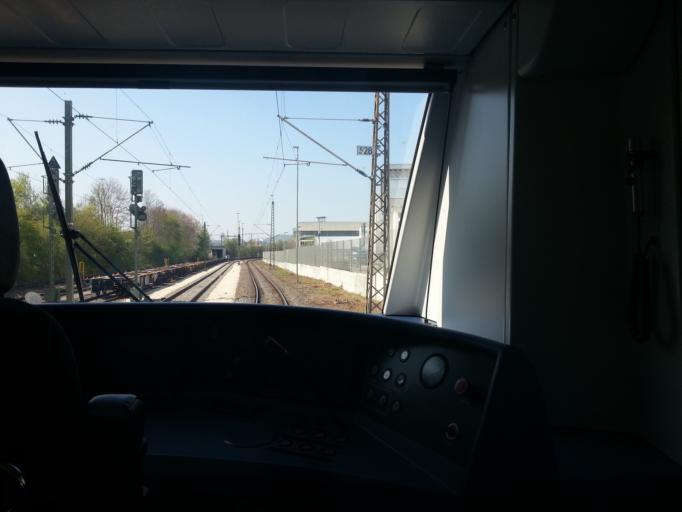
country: DE
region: Baden-Wuerttemberg
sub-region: Regierungsbezirk Stuttgart
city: Stuttgart-Ost
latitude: 48.7944
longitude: 9.2367
